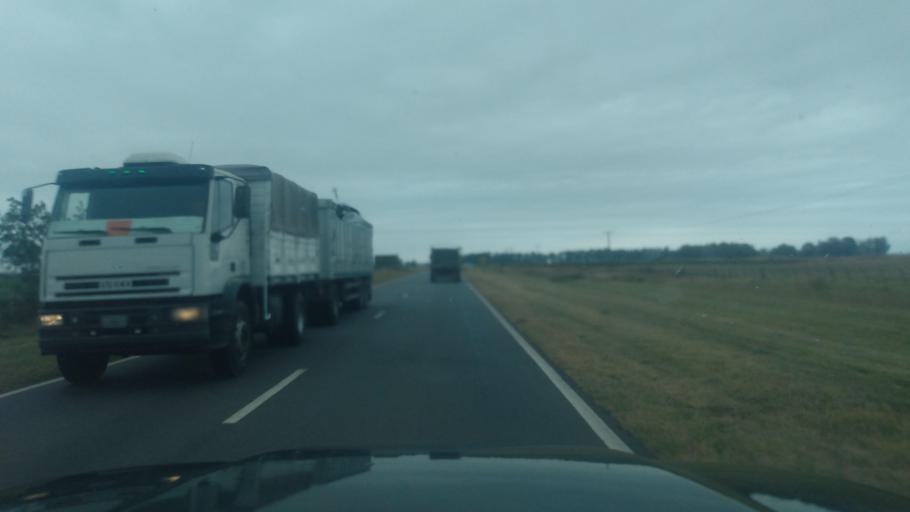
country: AR
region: Buenos Aires
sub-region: Partido de Nueve de Julio
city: Nueve de Julio
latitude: -35.4136
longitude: -60.7798
